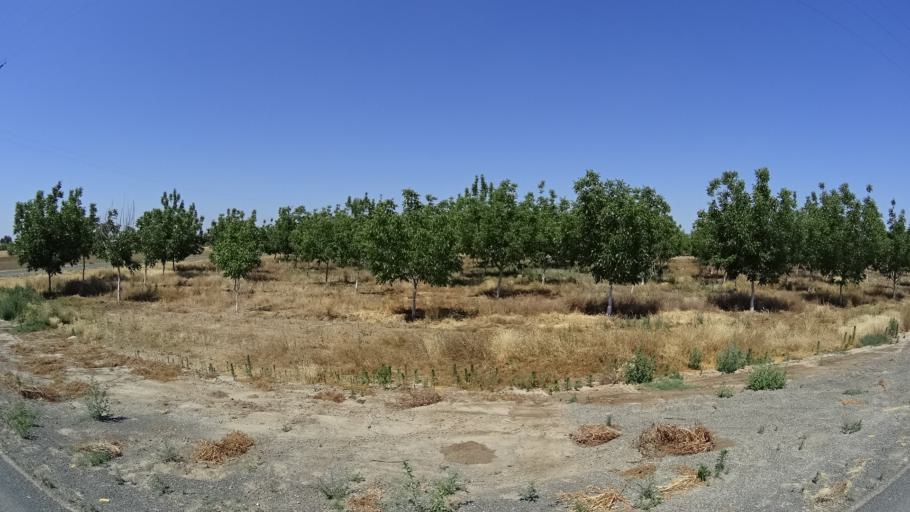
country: US
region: California
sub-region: Kings County
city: Lucerne
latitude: 36.4312
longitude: -119.6186
